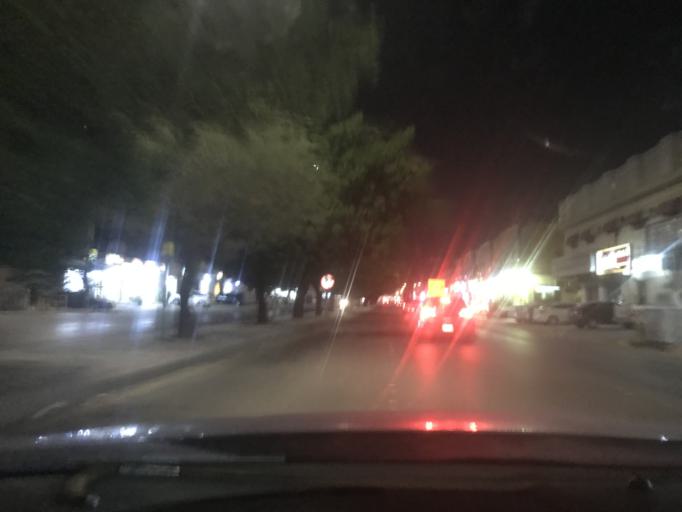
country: SA
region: Ar Riyad
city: Riyadh
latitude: 24.7384
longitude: 46.7766
